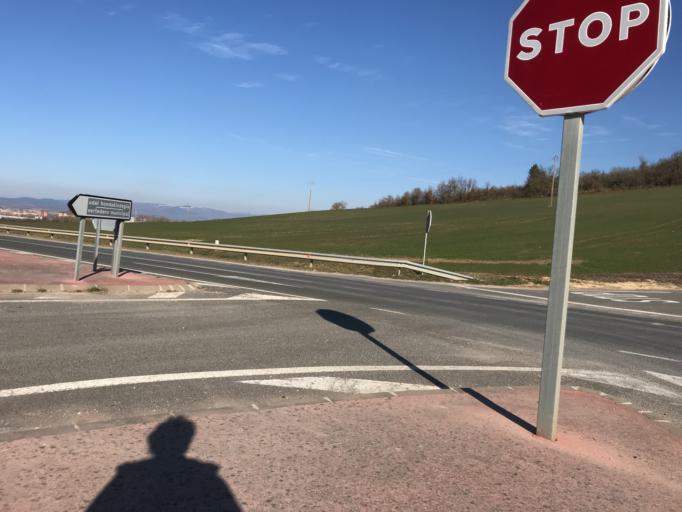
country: ES
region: Basque Country
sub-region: Provincia de Alava
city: Gasteiz / Vitoria
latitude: 42.8145
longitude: -2.6809
